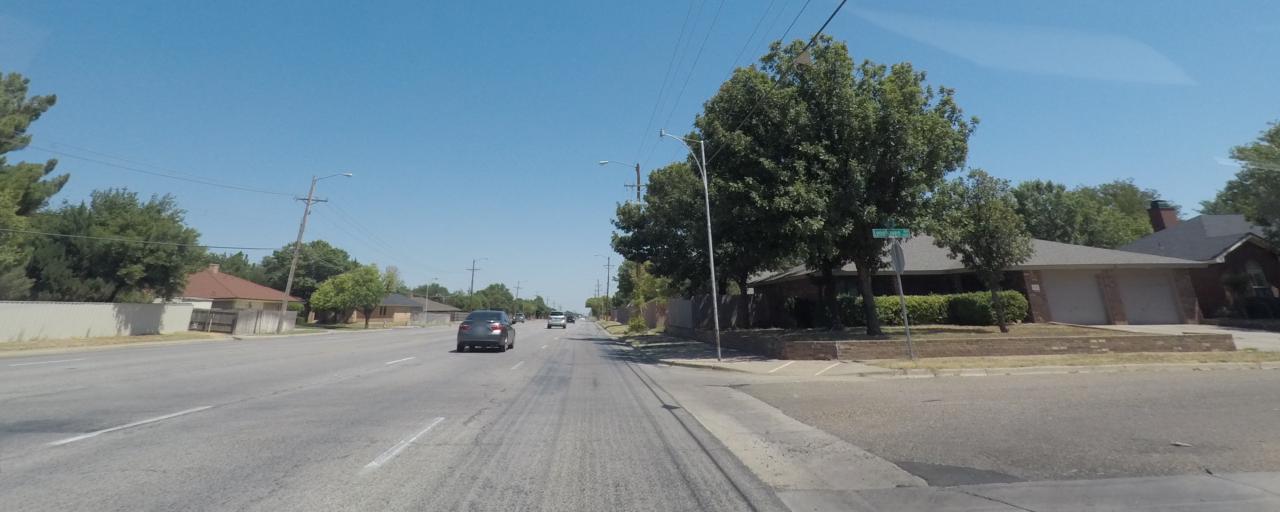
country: US
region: Texas
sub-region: Lubbock County
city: Lubbock
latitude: 33.5052
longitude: -101.8954
